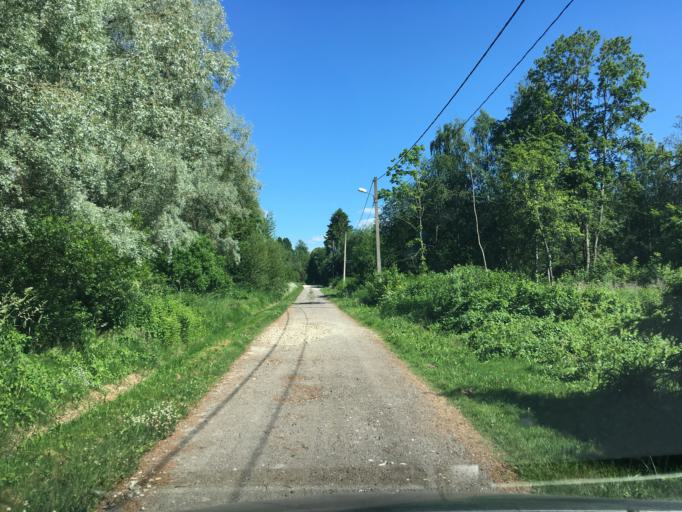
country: EE
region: Harju
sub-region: Raasiku vald
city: Raasiku
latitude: 59.3648
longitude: 25.1784
